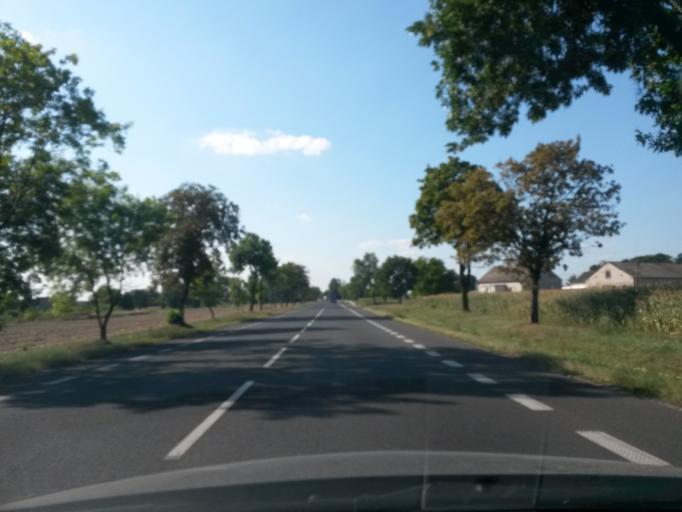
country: PL
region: Masovian Voivodeship
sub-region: Powiat sierpecki
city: Rosciszewo
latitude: 52.8202
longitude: 19.7786
